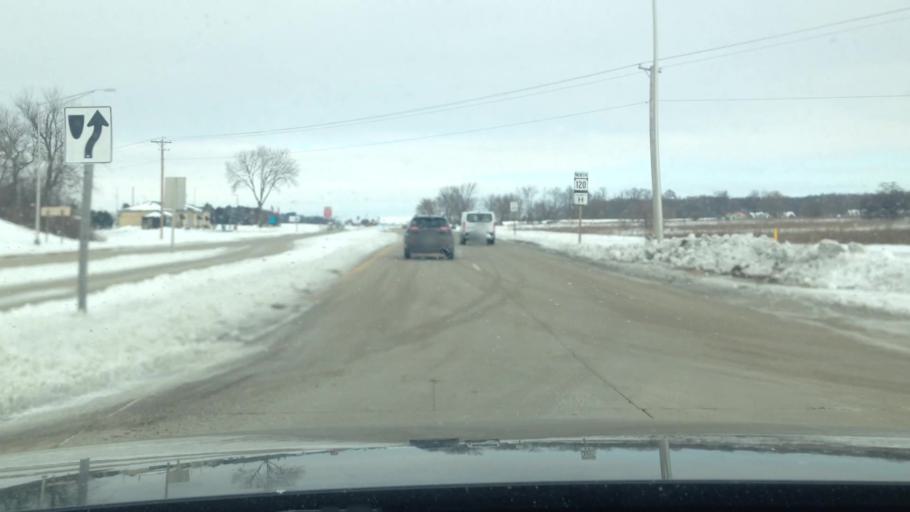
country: US
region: Wisconsin
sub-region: Walworth County
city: Lake Geneva
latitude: 42.5748
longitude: -88.4117
